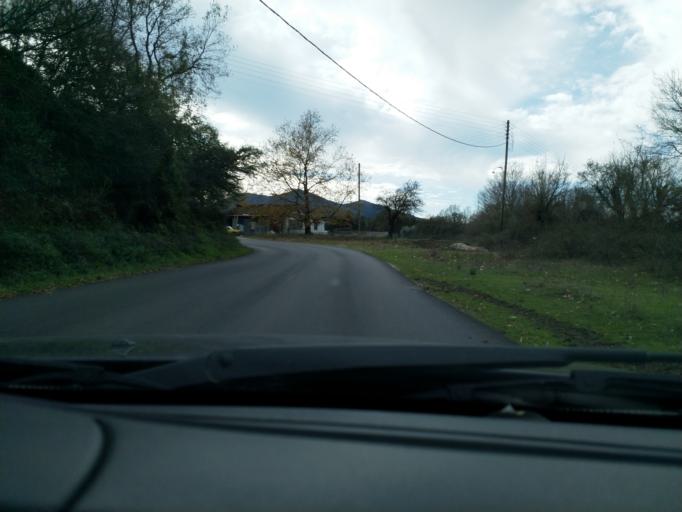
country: GR
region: Epirus
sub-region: Nomos Prevezis
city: Filippiada
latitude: 39.2184
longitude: 20.8576
